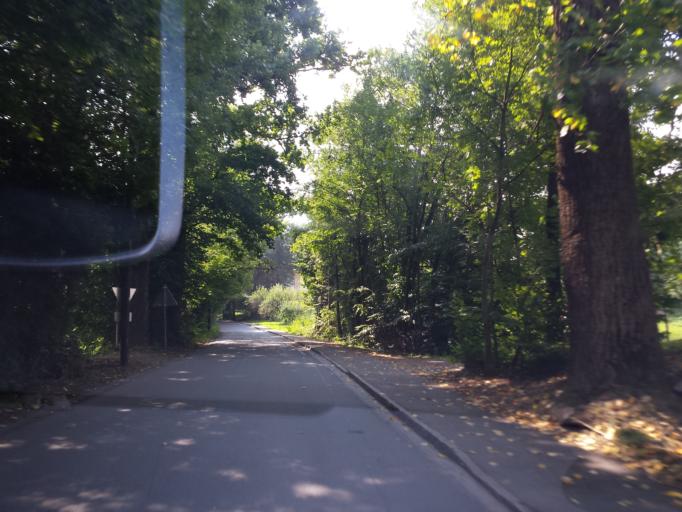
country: AT
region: Styria
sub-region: Politischer Bezirk Deutschlandsberg
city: Deutschlandsberg
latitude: 46.8155
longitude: 15.2429
